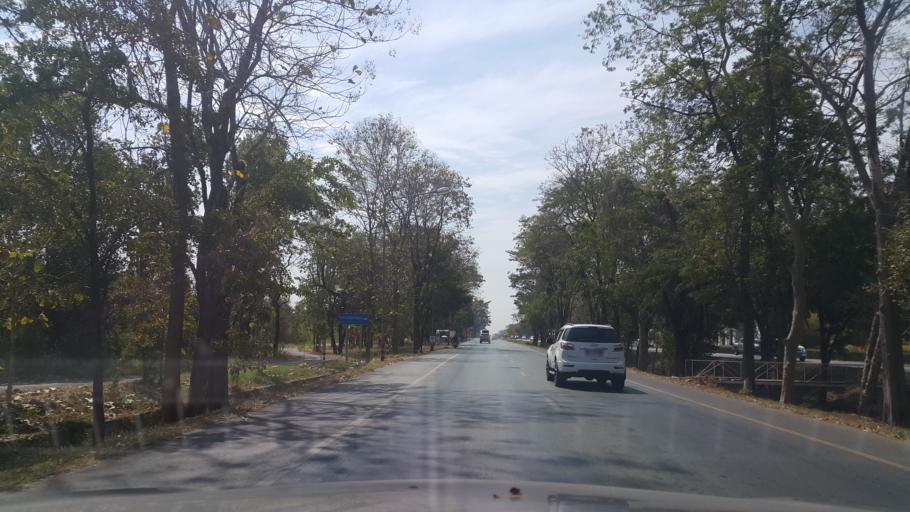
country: TH
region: Nakhon Ratchasima
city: Nakhon Ratchasima
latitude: 14.8665
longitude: 102.0717
